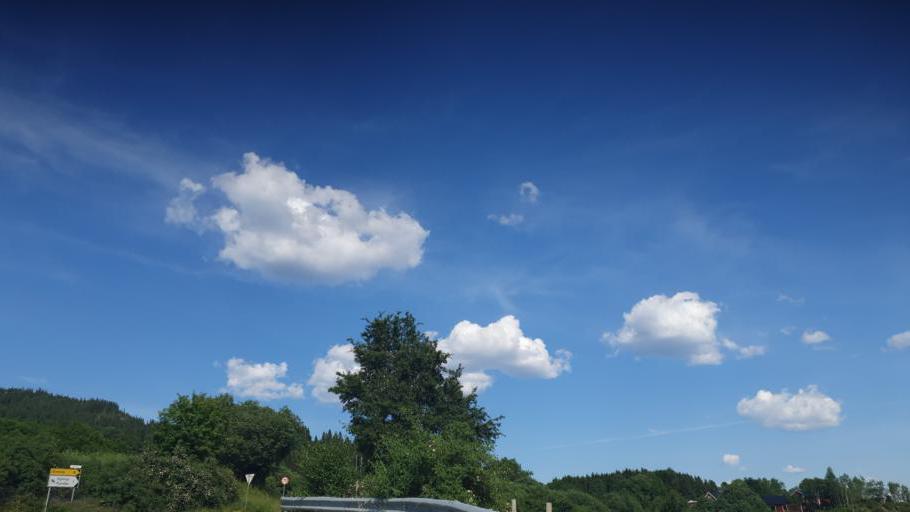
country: NO
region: Nord-Trondelag
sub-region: Leksvik
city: Leksvik
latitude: 63.6769
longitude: 10.6384
